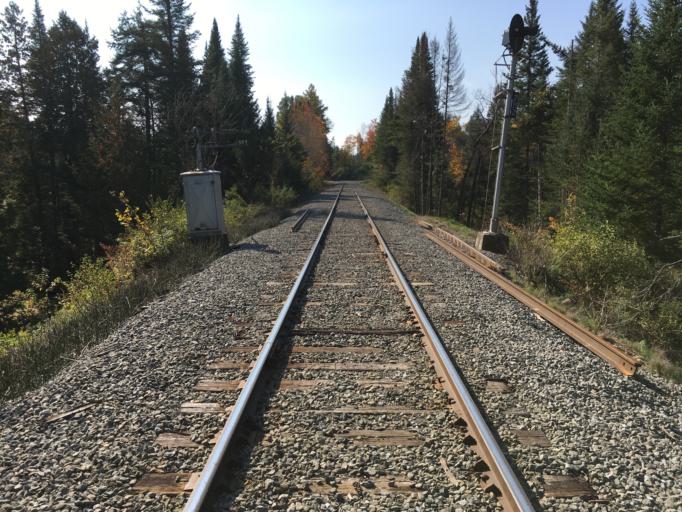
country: US
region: Vermont
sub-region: Caledonia County
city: Lyndonville
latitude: 44.6086
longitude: -71.9682
